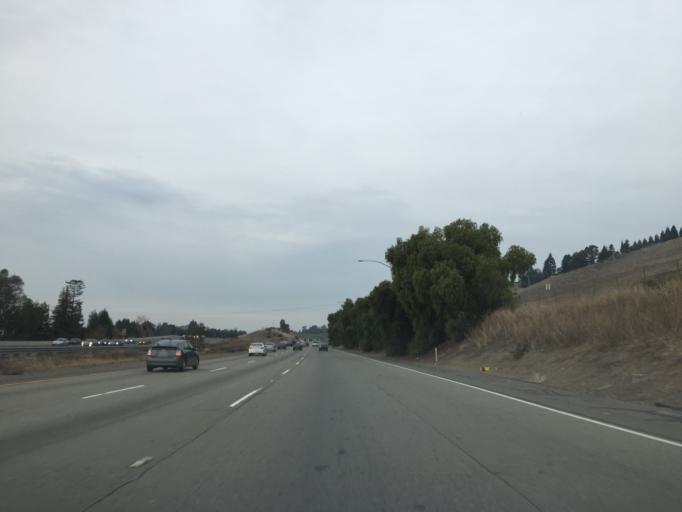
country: US
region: California
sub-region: Alameda County
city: Fremont
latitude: 37.5187
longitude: -121.9418
